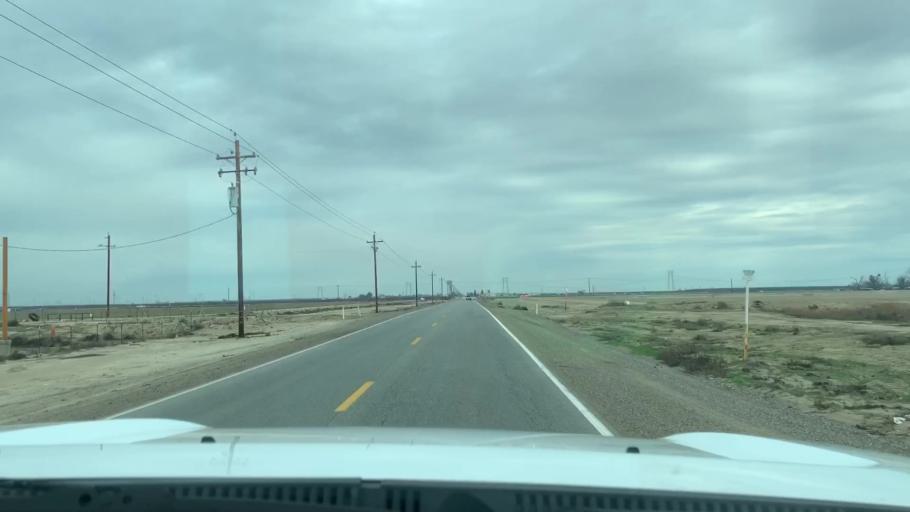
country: US
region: California
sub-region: Kern County
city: Rosedale
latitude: 35.3493
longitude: -119.2522
